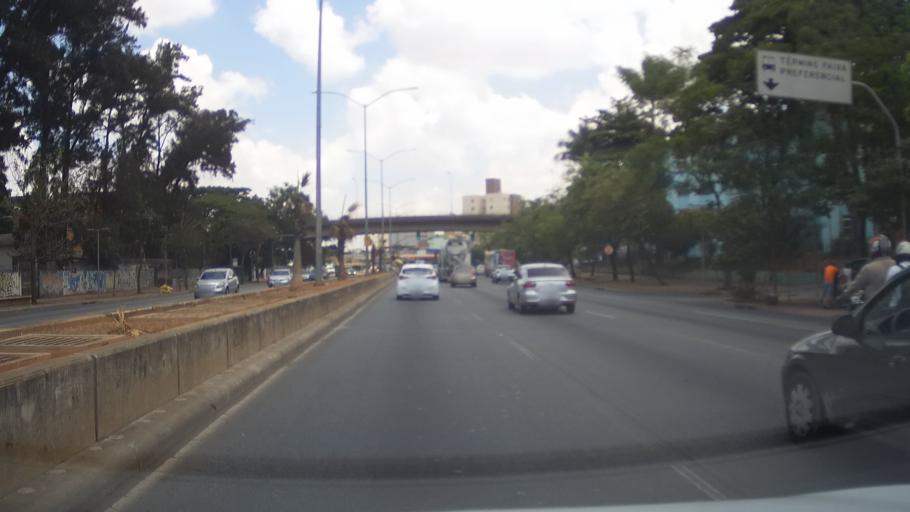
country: BR
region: Minas Gerais
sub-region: Belo Horizonte
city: Belo Horizonte
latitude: -19.9180
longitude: -43.9672
